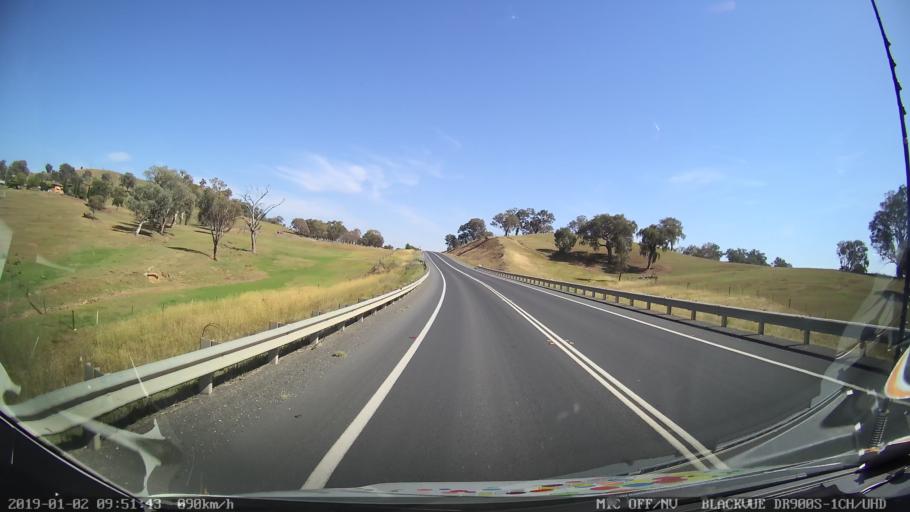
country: AU
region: New South Wales
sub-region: Tumut Shire
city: Tumut
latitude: -35.2698
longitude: 148.2113
